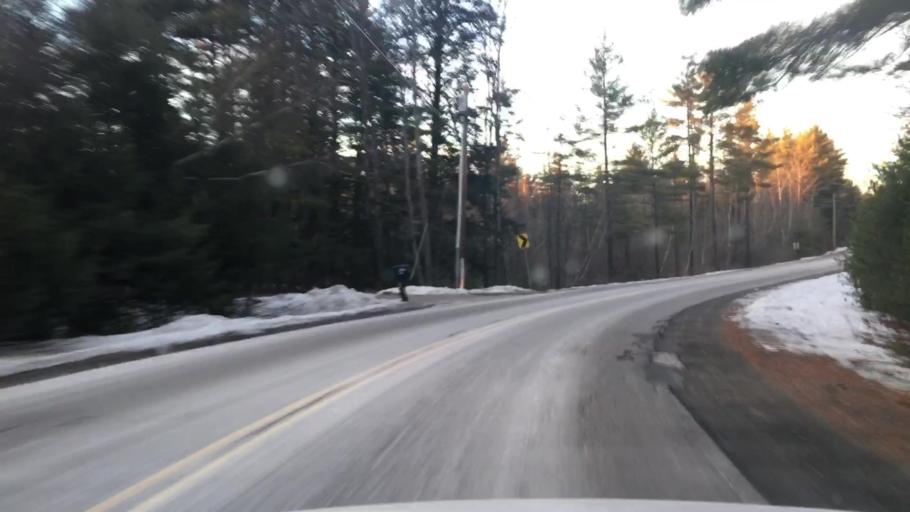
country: US
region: Maine
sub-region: York County
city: Lebanon
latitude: 43.3395
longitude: -70.8653
